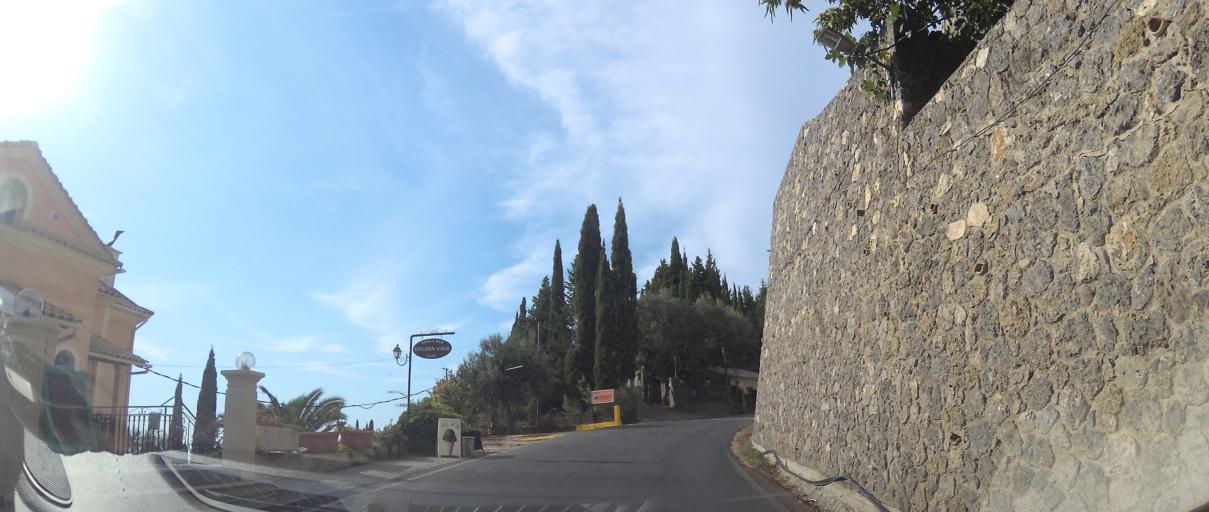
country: GR
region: Ionian Islands
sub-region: Nomos Kerkyras
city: Kynopiastes
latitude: 39.5523
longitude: 19.8624
